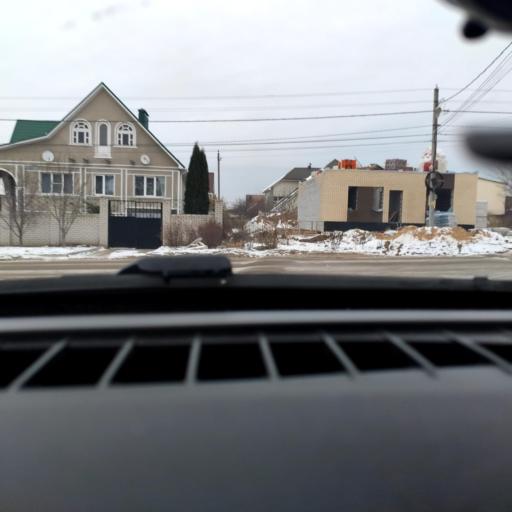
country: RU
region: Voronezj
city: Podgornoye
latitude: 51.7240
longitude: 39.1396
